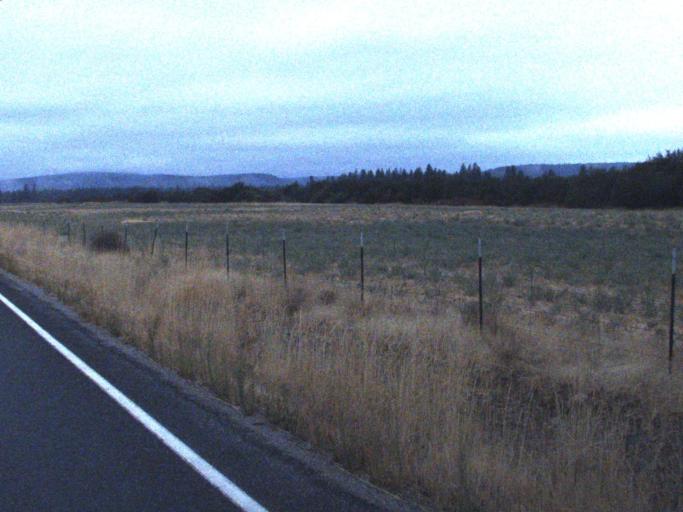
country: US
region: Washington
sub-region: Spokane County
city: Deer Park
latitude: 47.9233
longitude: -117.7827
